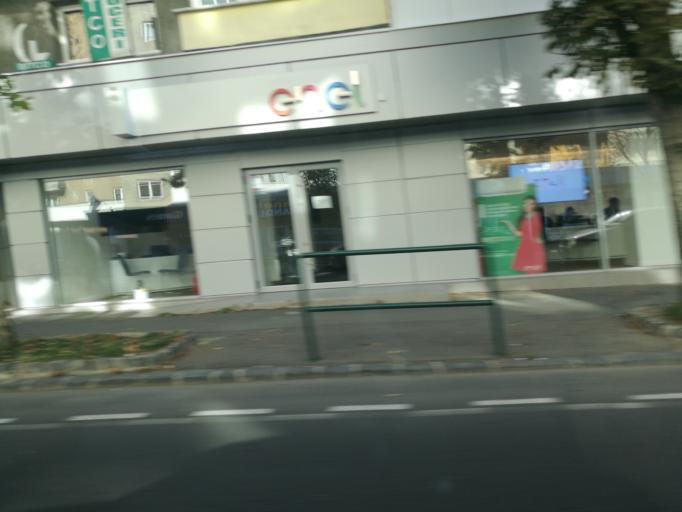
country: RO
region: Brasov
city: Brasov
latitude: 45.6569
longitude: 25.5987
